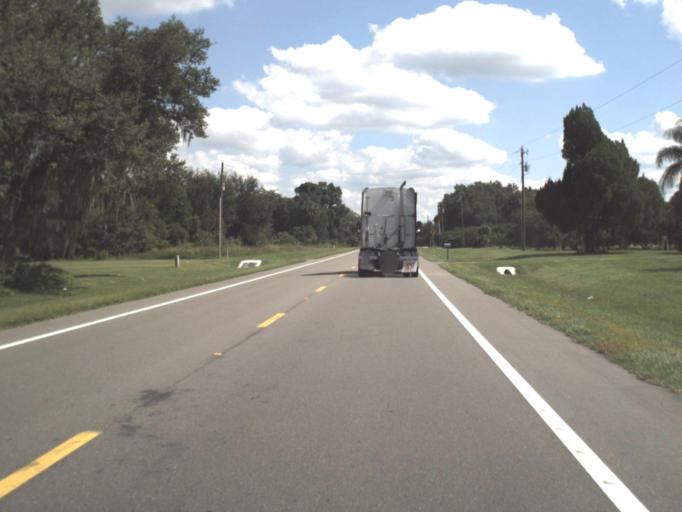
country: US
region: Florida
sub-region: Hardee County
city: Zolfo Springs
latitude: 27.4881
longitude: -81.7477
